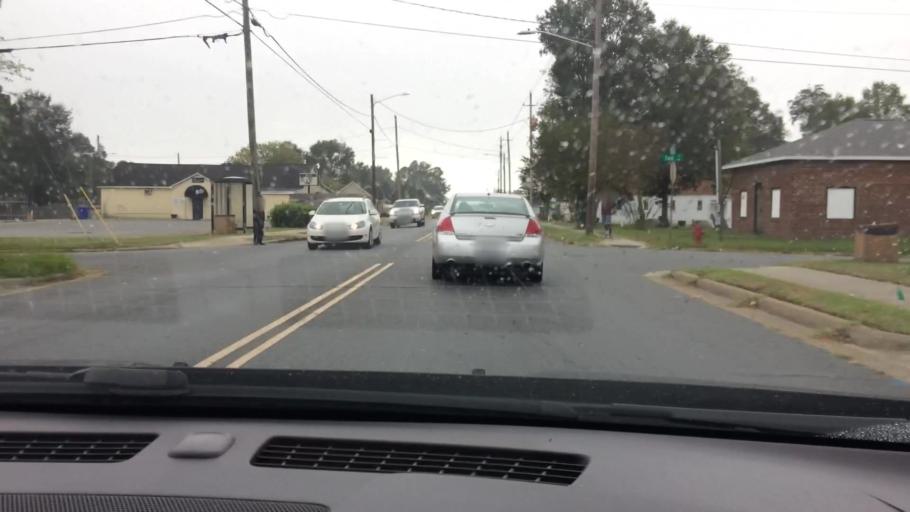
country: US
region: North Carolina
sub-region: Pitt County
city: Greenville
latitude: 35.6130
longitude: -77.3875
